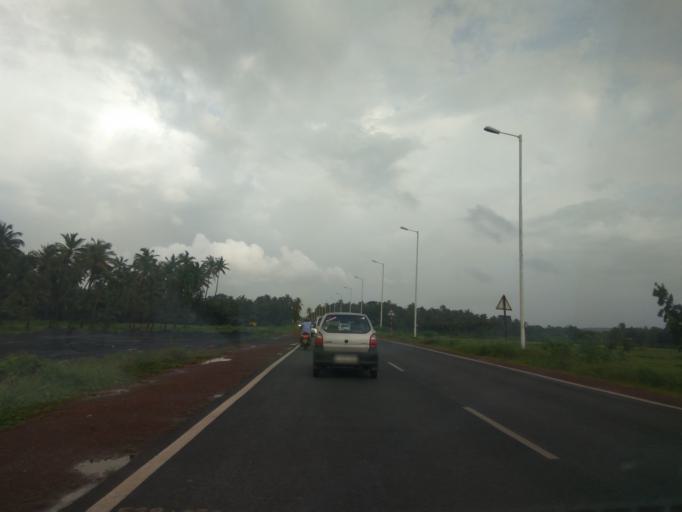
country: IN
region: Goa
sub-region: North Goa
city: Goa Velha
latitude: 15.4284
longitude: 73.8917
